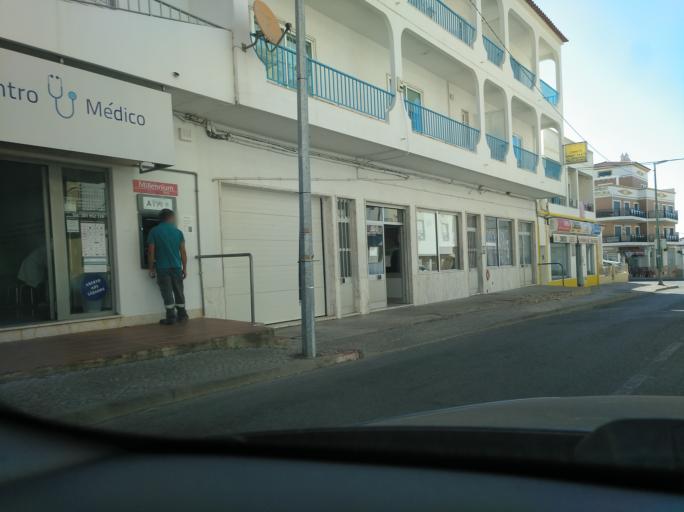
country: PT
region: Faro
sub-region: Vila Real de Santo Antonio
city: Monte Gordo
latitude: 37.1757
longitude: -7.5336
